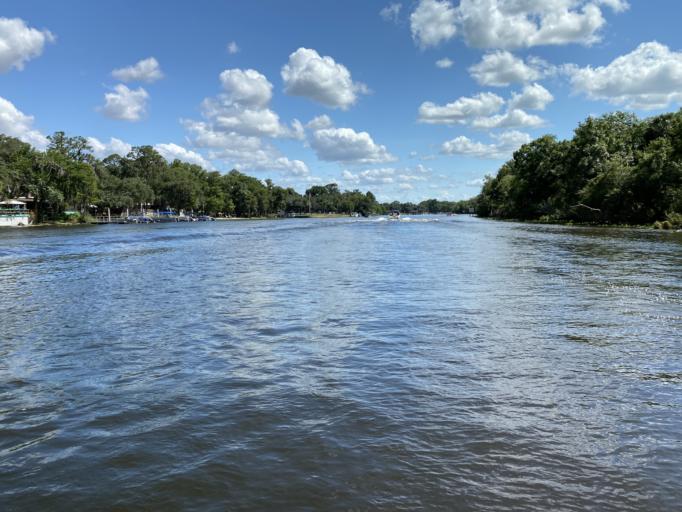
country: US
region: Florida
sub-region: Volusia County
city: DeBary
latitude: 28.8941
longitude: -81.3547
